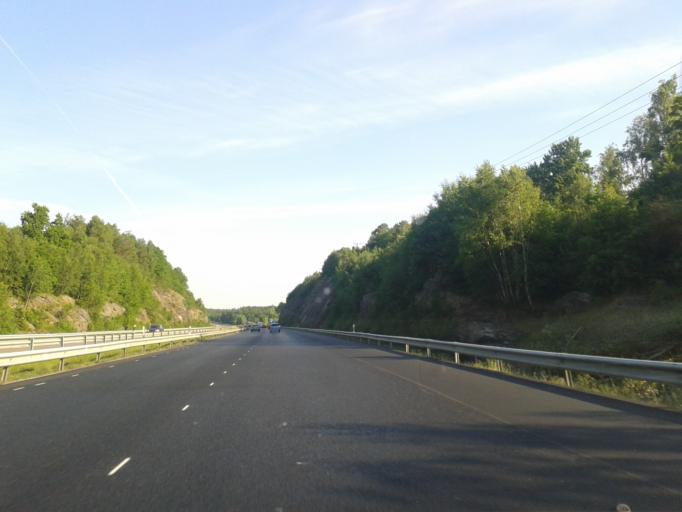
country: SE
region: Vaestra Goetaland
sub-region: Kungalvs Kommun
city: Kode
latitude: 57.9294
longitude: 11.8746
